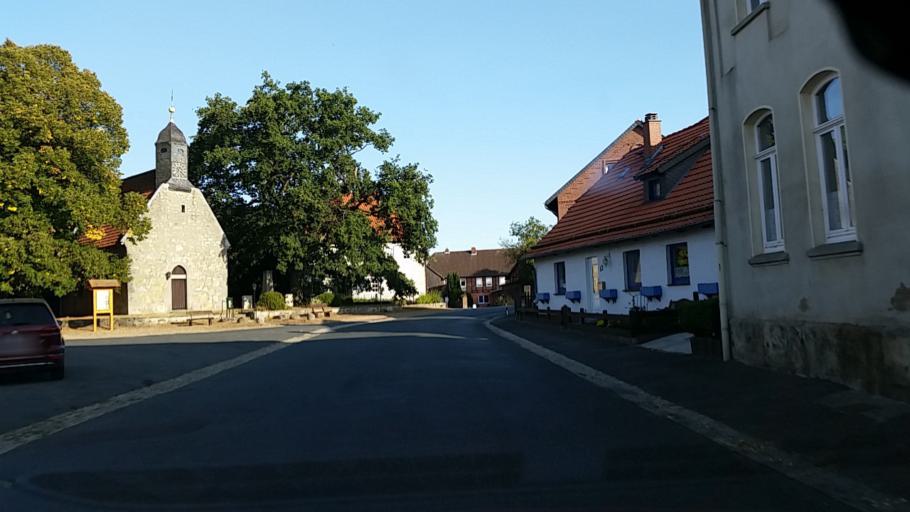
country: DE
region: Lower Saxony
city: Konigslutter am Elm
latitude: 52.3021
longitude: 10.7657
